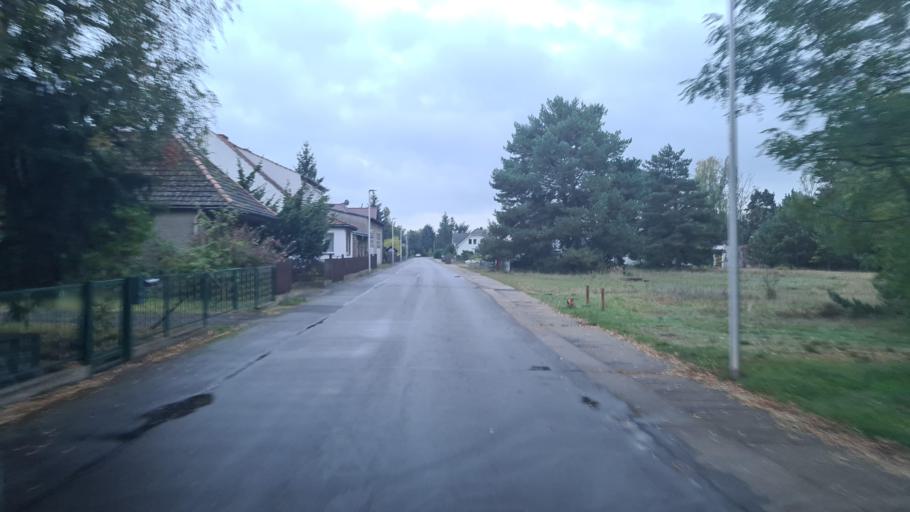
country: DE
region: Brandenburg
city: Munchehofe
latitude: 52.1251
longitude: 13.9471
